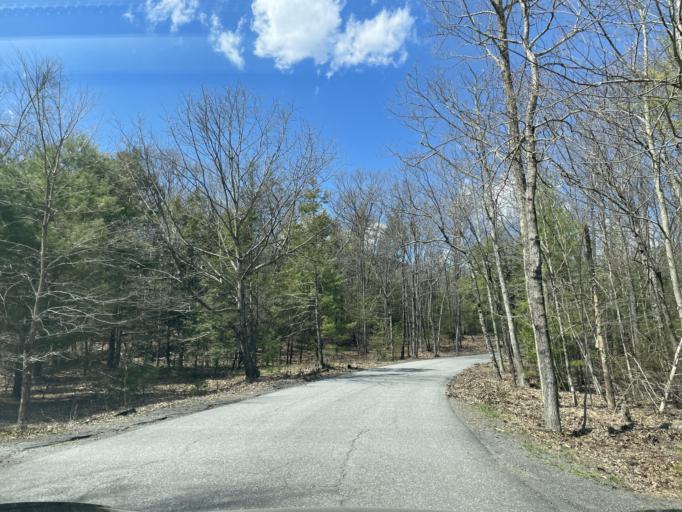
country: US
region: New York
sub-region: Ulster County
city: Zena
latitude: 42.0654
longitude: -74.0700
